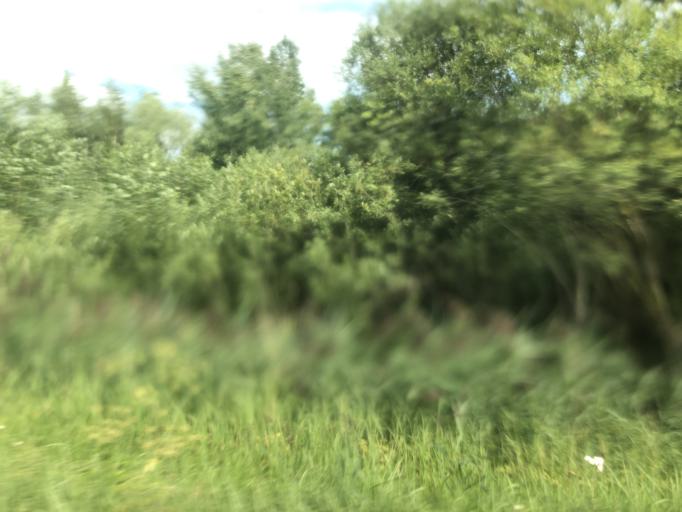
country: LV
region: Vecumnieki
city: Vecumnieki
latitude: 56.4572
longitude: 24.6344
